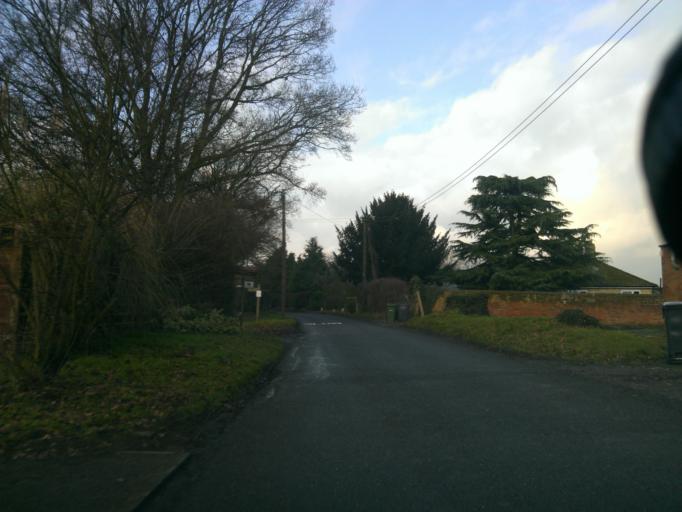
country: GB
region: England
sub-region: Suffolk
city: Sudbury
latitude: 51.9891
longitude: 0.7519
